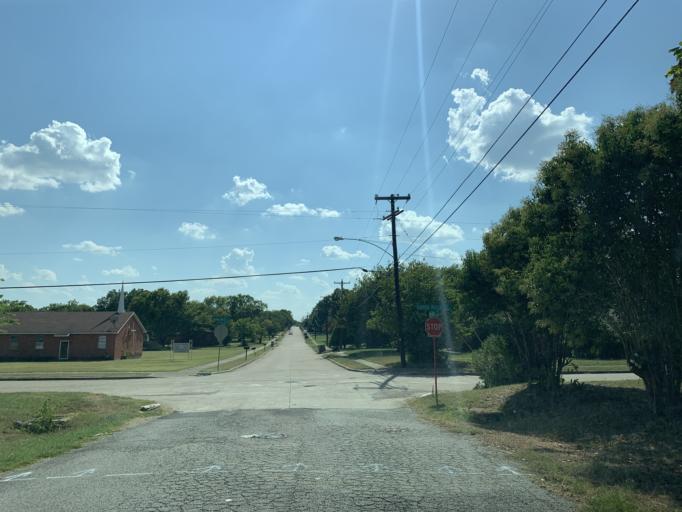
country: US
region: Texas
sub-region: Dallas County
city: Hutchins
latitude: 32.6539
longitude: -96.7768
